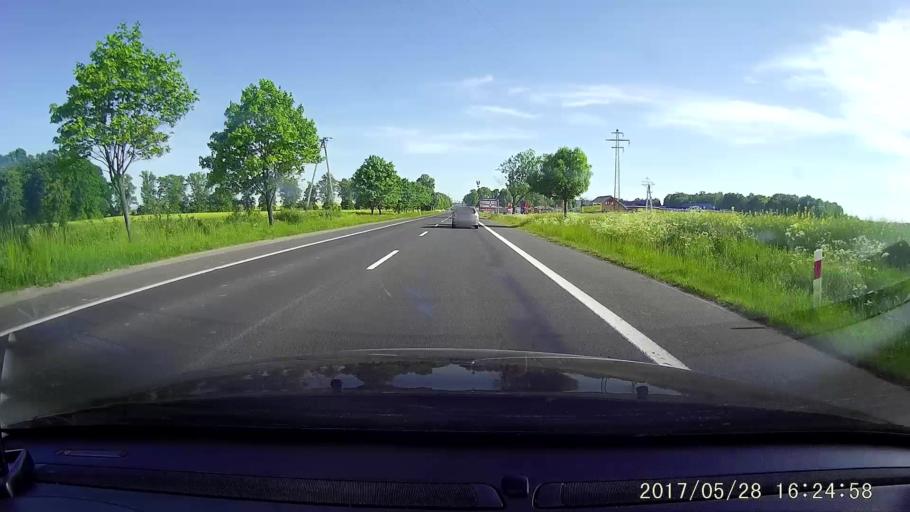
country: PL
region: Lower Silesian Voivodeship
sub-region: Powiat zgorzelecki
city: Lagow
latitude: 51.1657
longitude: 15.0296
